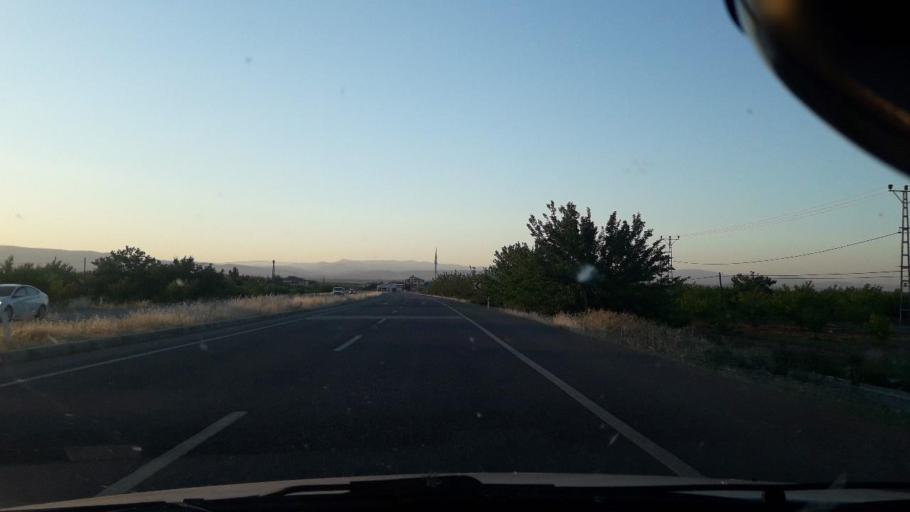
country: TR
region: Malatya
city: Yazihan
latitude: 38.4629
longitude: 38.2281
